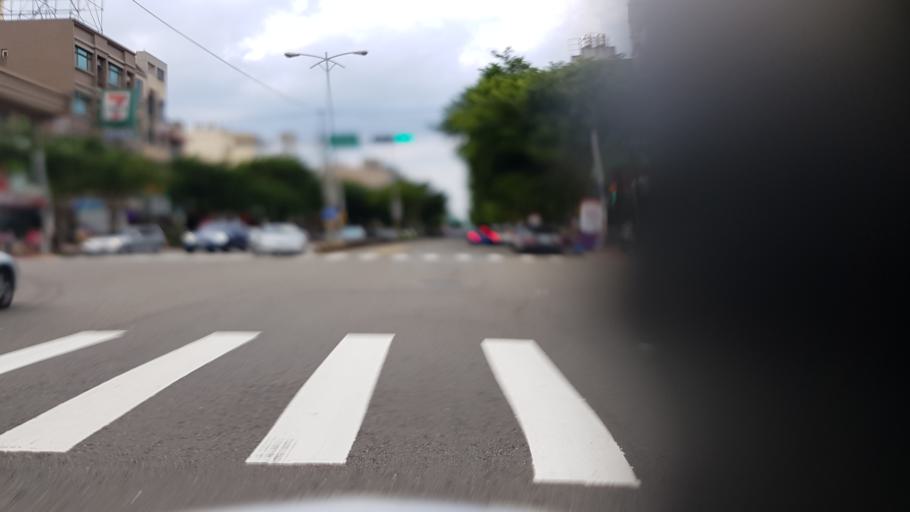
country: TW
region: Taiwan
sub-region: Hsinchu
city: Zhubei
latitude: 24.8102
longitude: 121.0294
